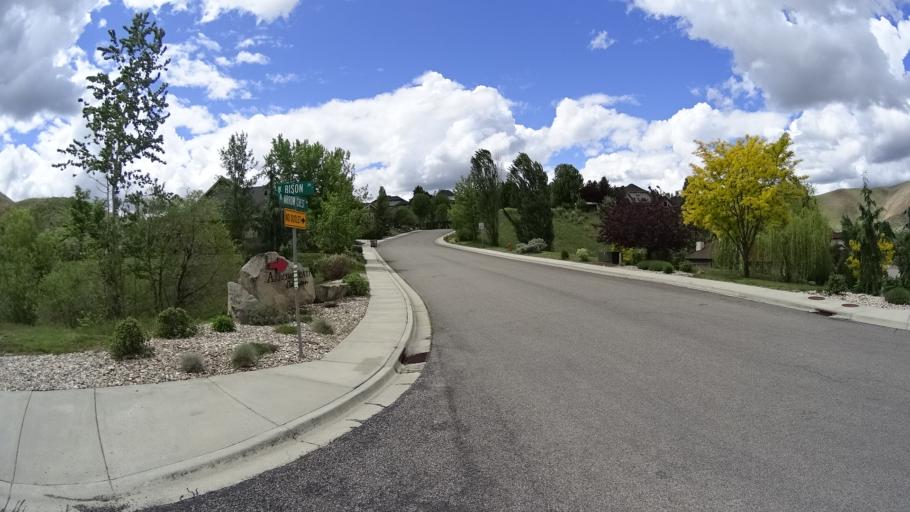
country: US
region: Idaho
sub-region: Ada County
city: Garden City
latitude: 43.6652
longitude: -116.2119
